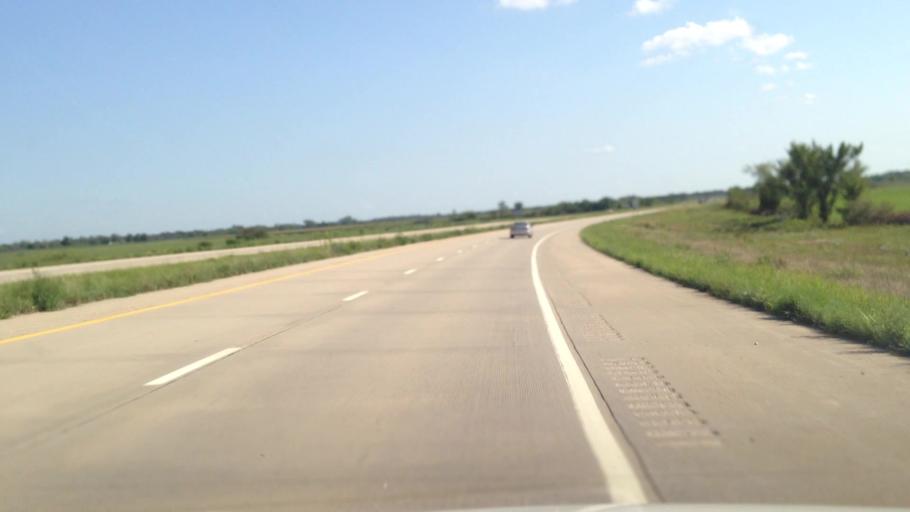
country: US
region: Kansas
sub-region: Bourbon County
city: Fort Scott
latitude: 37.9286
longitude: -94.7052
